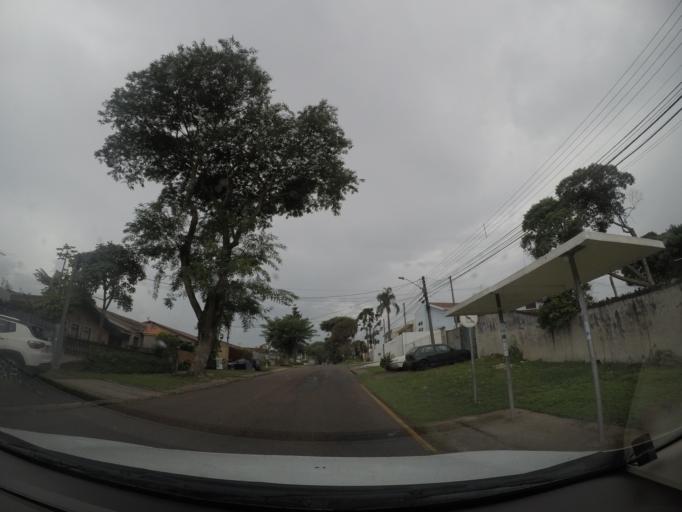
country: BR
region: Parana
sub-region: Sao Jose Dos Pinhais
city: Sao Jose dos Pinhais
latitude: -25.5120
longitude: -49.2474
